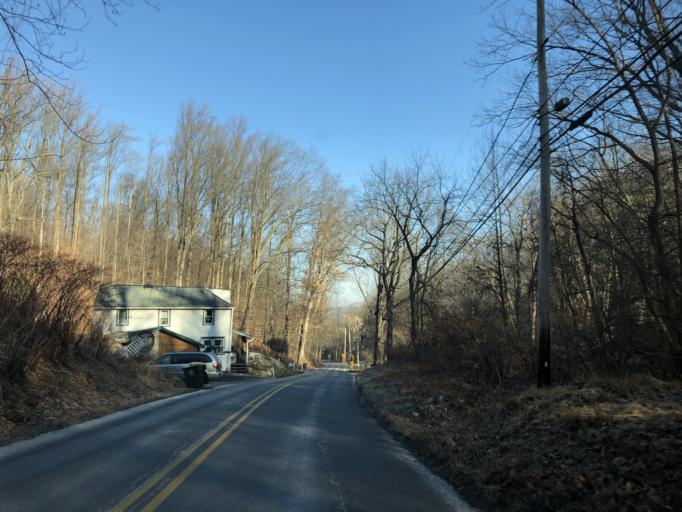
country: US
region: Pennsylvania
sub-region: Chester County
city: Downingtown
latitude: 39.9925
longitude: -75.7122
